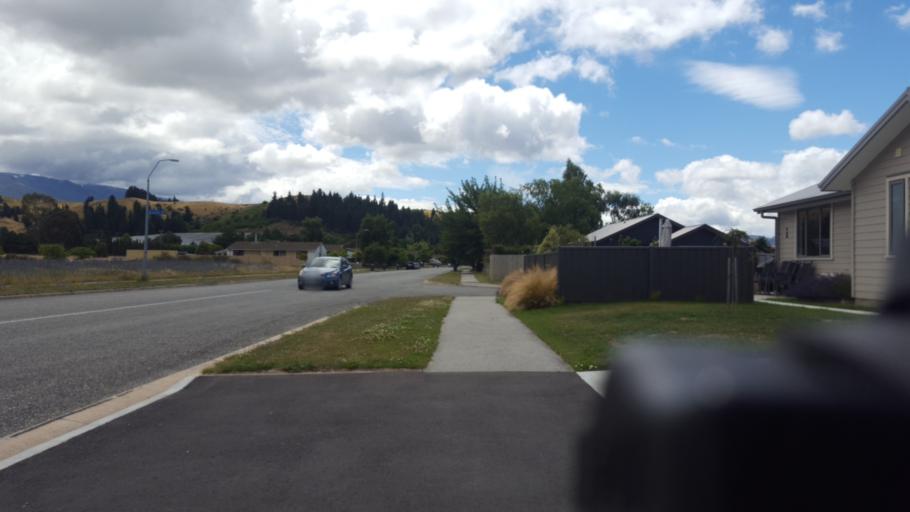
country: NZ
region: Otago
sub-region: Queenstown-Lakes District
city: Wanaka
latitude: -45.0422
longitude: 169.1802
